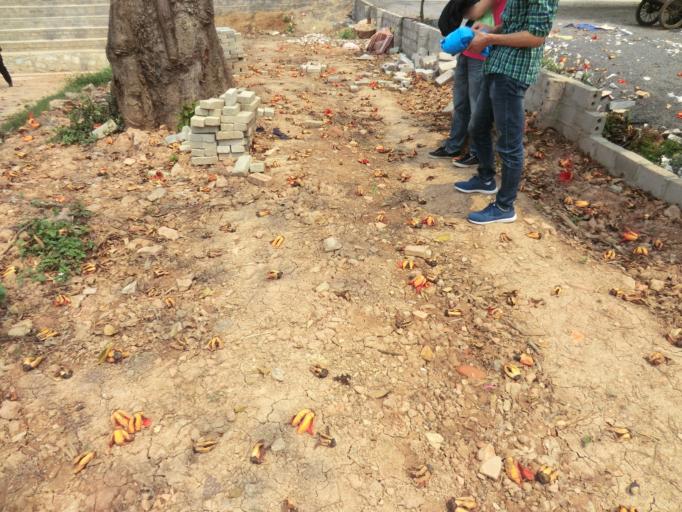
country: VN
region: Ha Noi
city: Chuc Son
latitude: 20.9389
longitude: 105.6952
